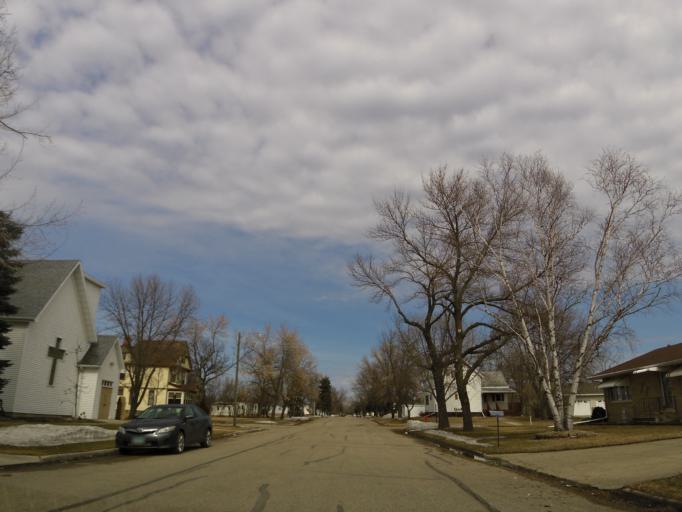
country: US
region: North Dakota
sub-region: Walsh County
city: Grafton
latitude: 48.2900
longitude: -97.3746
